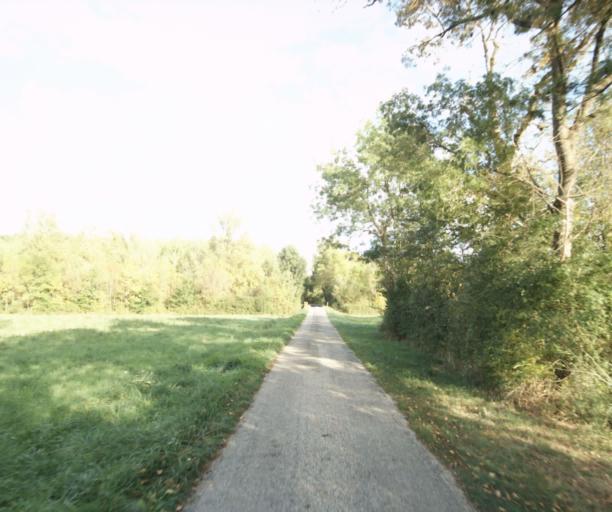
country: FR
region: Midi-Pyrenees
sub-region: Departement du Gers
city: Gondrin
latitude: 43.8900
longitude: 0.2964
